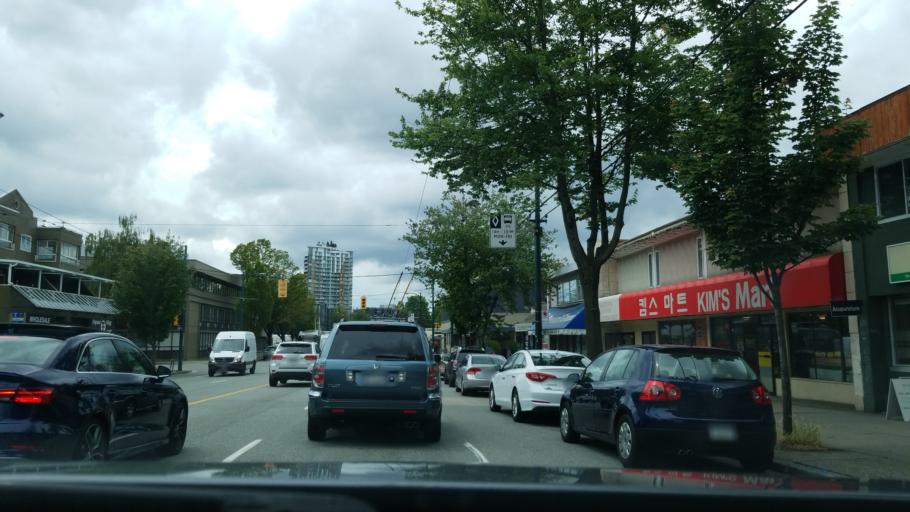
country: CA
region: British Columbia
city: Vancouver
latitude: 49.2625
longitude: -123.0921
